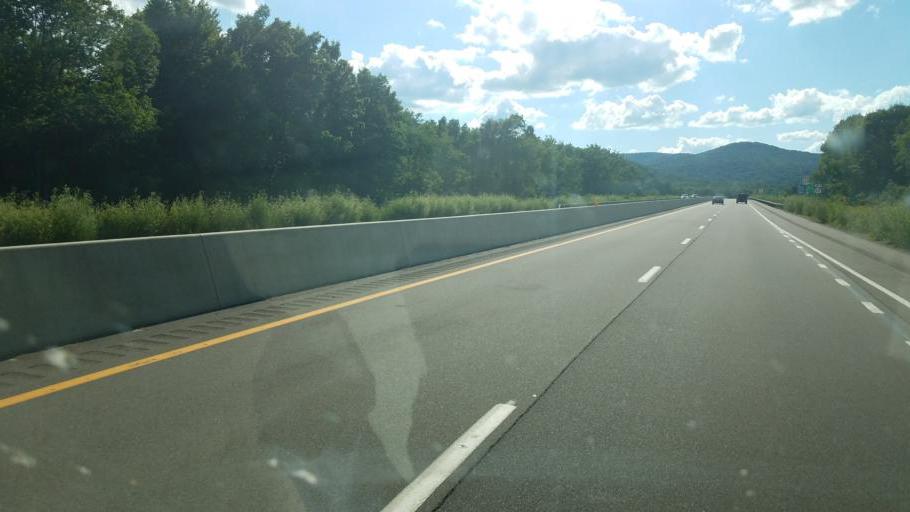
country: US
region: New York
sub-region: Cattaraugus County
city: Salamanca
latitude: 42.0898
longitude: -78.6387
